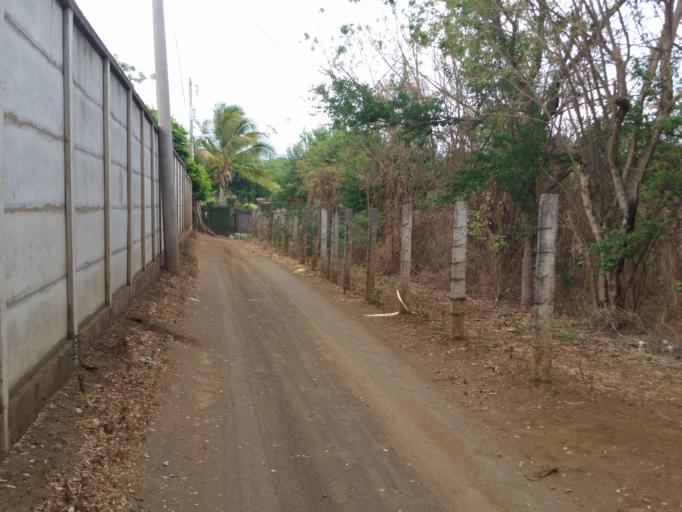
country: NI
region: Managua
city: Managua
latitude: 12.0805
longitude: -86.2506
